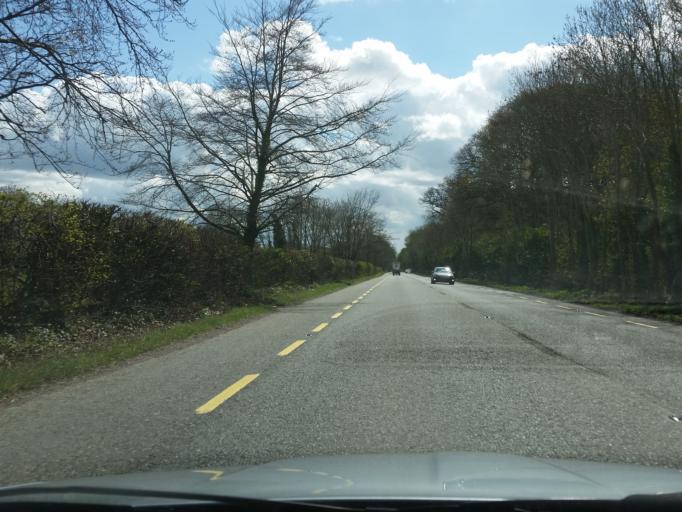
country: IE
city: Kentstown
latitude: 53.6335
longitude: -6.4937
